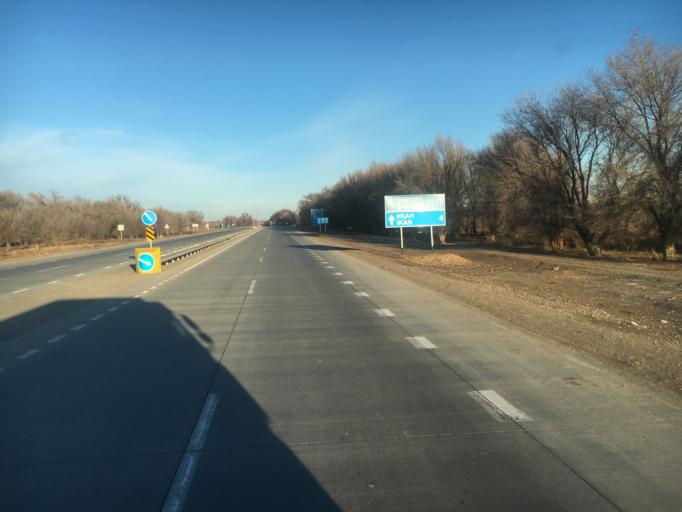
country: KZ
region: Ongtustik Qazaqstan
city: Turkestan
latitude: 43.1493
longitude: 68.5741
